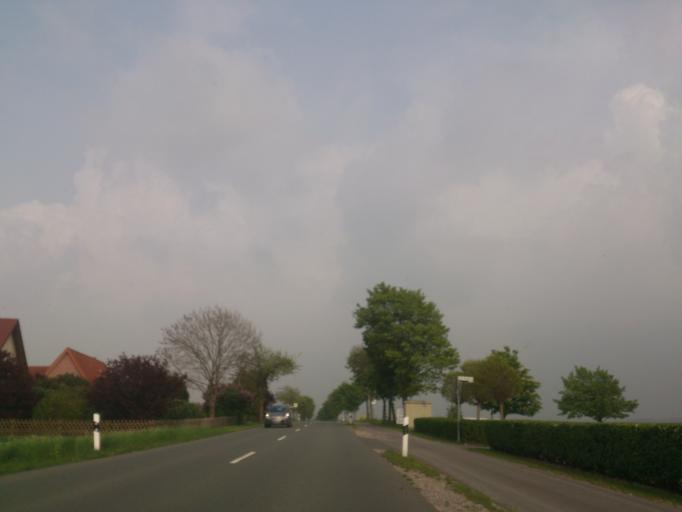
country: DE
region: North Rhine-Westphalia
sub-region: Regierungsbezirk Detmold
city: Paderborn
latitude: 51.6986
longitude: 8.8280
